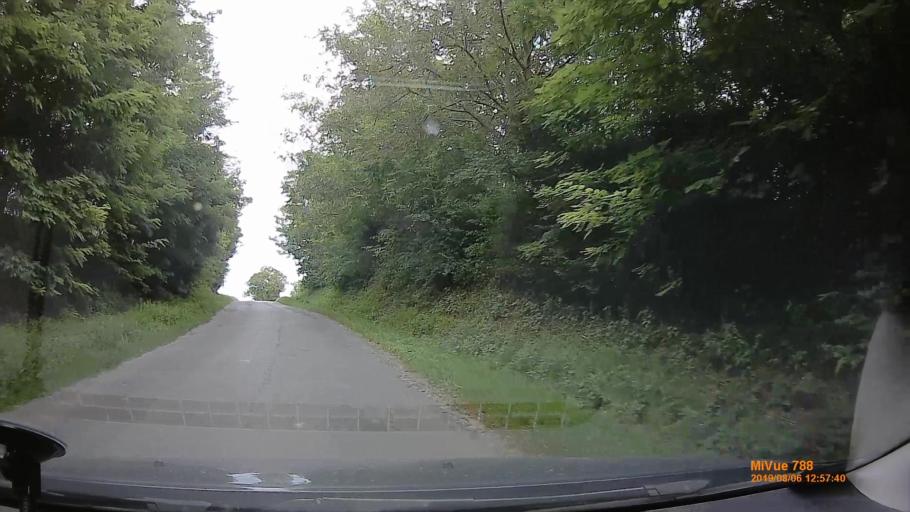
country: HU
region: Zala
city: Pacsa
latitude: 46.6308
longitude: 17.0418
